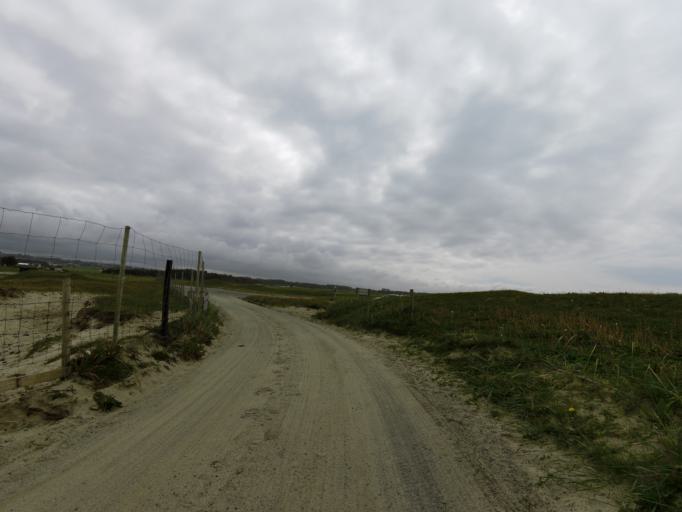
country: NO
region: Rogaland
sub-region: Klepp
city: Kleppe
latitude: 58.7995
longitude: 5.5513
